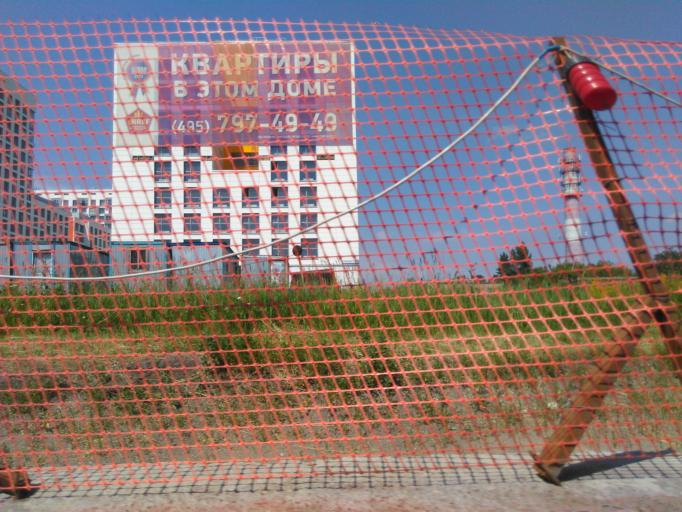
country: RU
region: Moskovskaya
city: Balashikha
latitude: 55.7967
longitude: 37.9646
